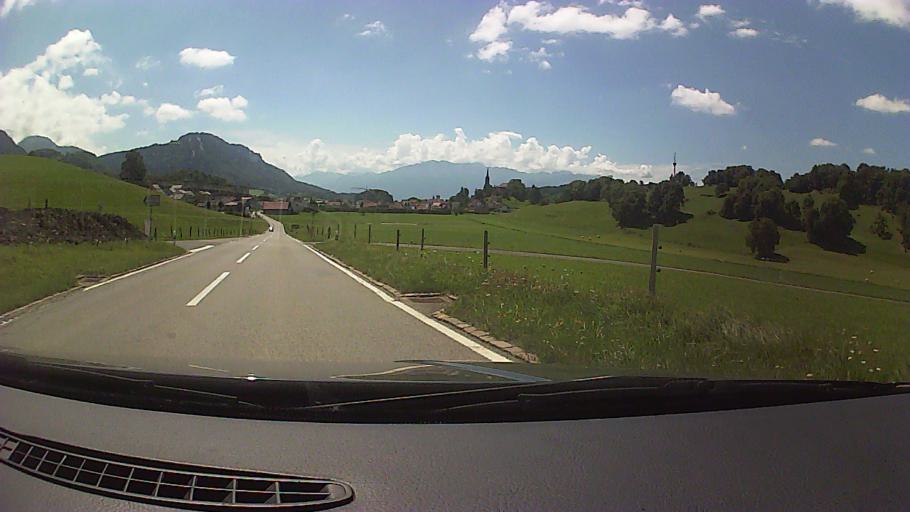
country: CH
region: Fribourg
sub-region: Veveyse District
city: Chatel-Saint-Denis
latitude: 46.5373
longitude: 6.9069
